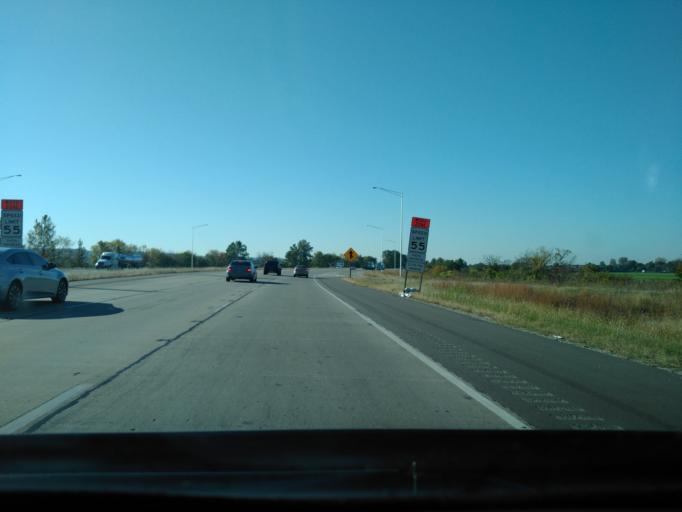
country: US
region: Illinois
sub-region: Saint Clair County
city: Caseyville
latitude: 38.6556
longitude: -90.0326
